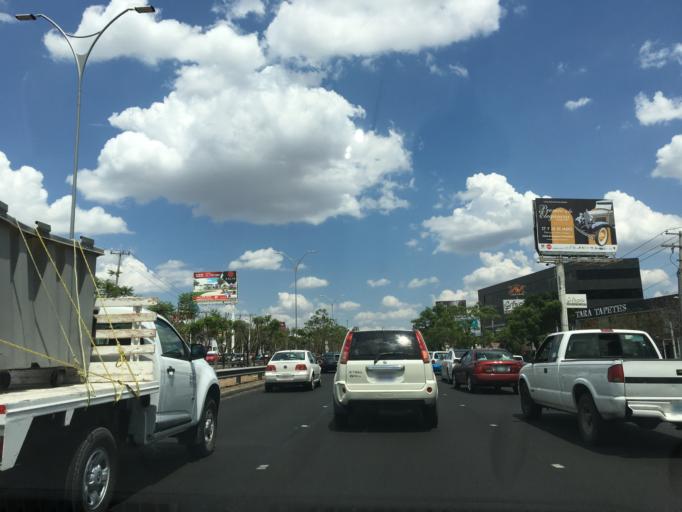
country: MX
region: Queretaro
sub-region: Queretaro
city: Santiago de Queretaro
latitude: 20.6143
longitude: -100.3863
